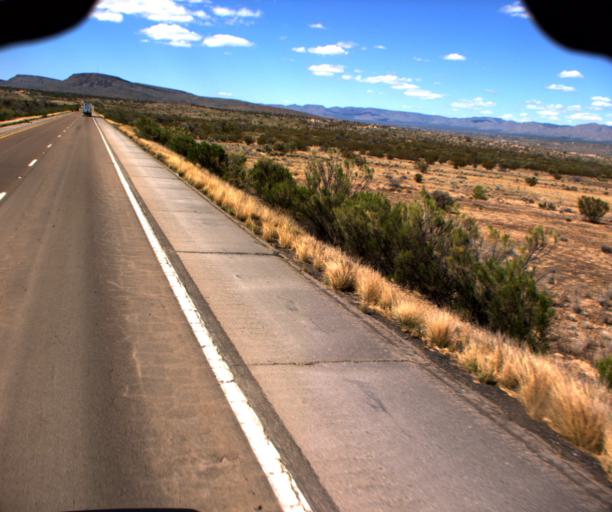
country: US
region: Arizona
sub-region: Mohave County
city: Kingman
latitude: 35.1169
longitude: -113.6661
